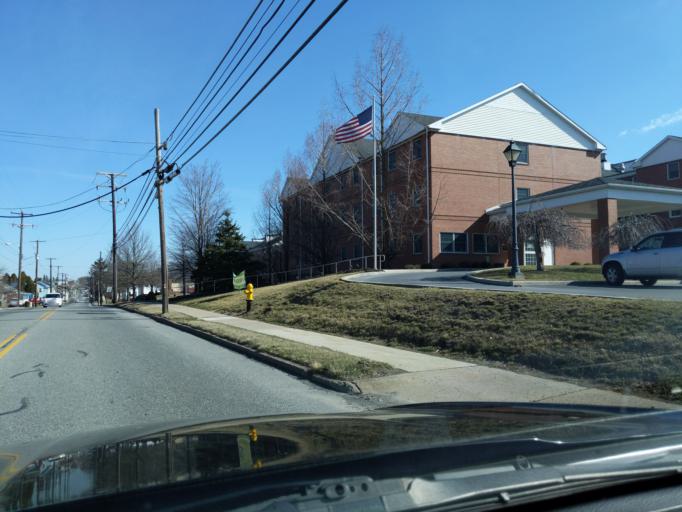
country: US
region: Pennsylvania
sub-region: Blair County
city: Martinsburg
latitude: 40.3048
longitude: -78.3286
